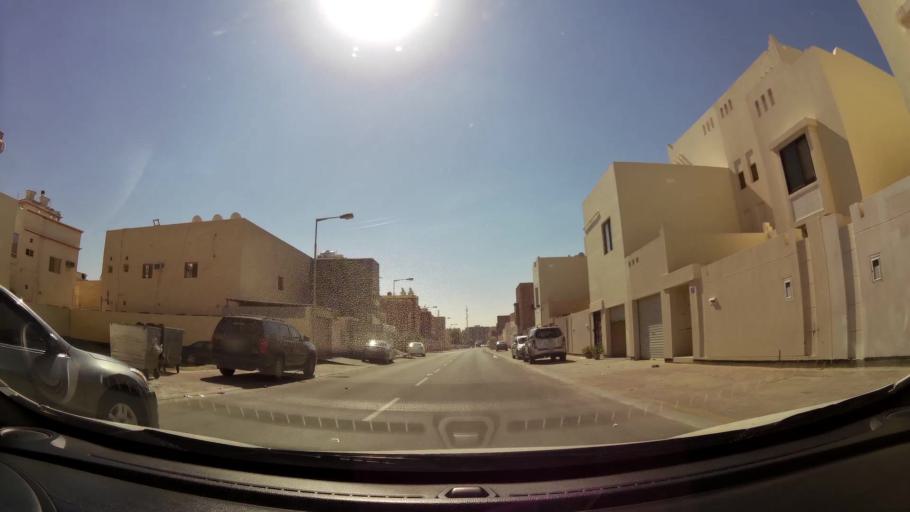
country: BH
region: Muharraq
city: Al Hadd
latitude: 26.2480
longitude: 50.6334
